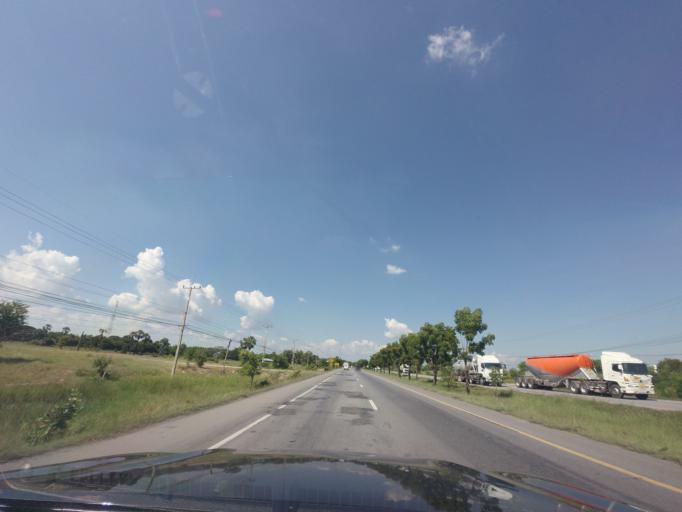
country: TH
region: Nakhon Ratchasima
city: Non Sung
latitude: 15.1790
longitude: 102.3379
